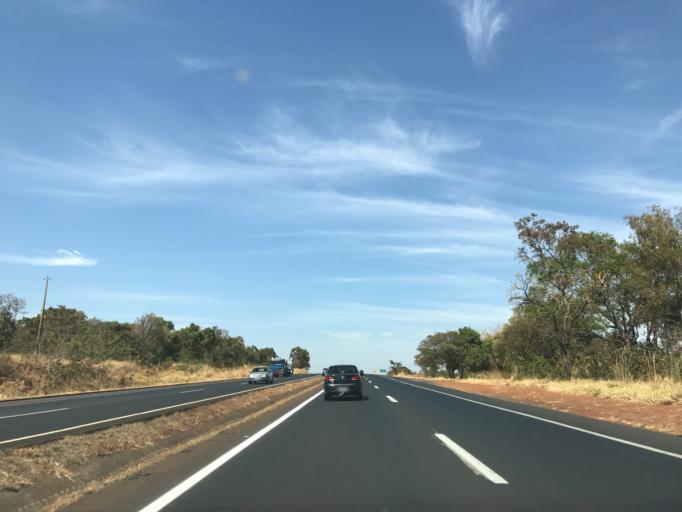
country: BR
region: Minas Gerais
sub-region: Monte Alegre De Minas
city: Monte Alegre de Minas
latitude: -18.8071
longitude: -49.0840
